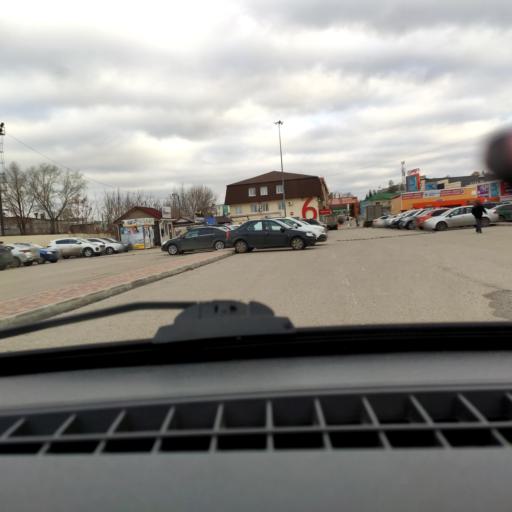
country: RU
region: Bashkortostan
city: Ufa
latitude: 54.8014
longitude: 56.0931
